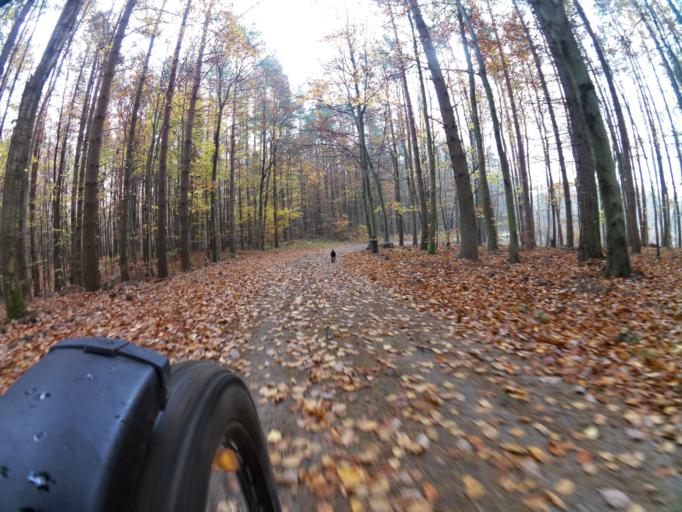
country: PL
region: Pomeranian Voivodeship
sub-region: Powiat pucki
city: Krokowa
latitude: 54.7723
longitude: 18.0929
